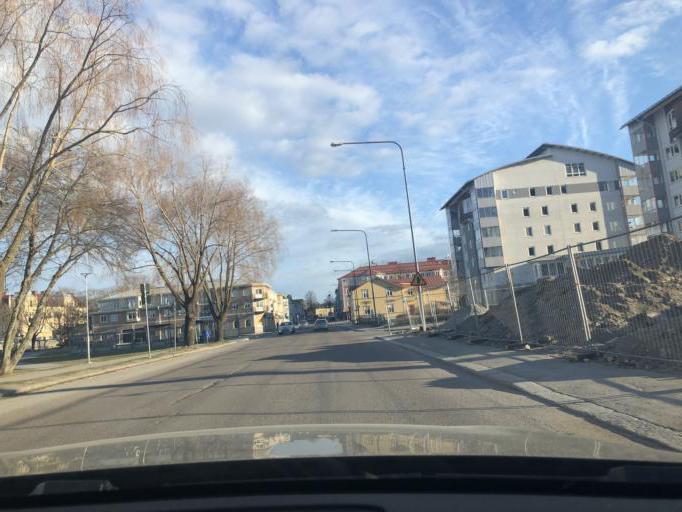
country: SE
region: Gaevleborg
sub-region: Hudiksvalls Kommun
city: Hudiksvall
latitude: 61.7302
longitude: 17.1050
